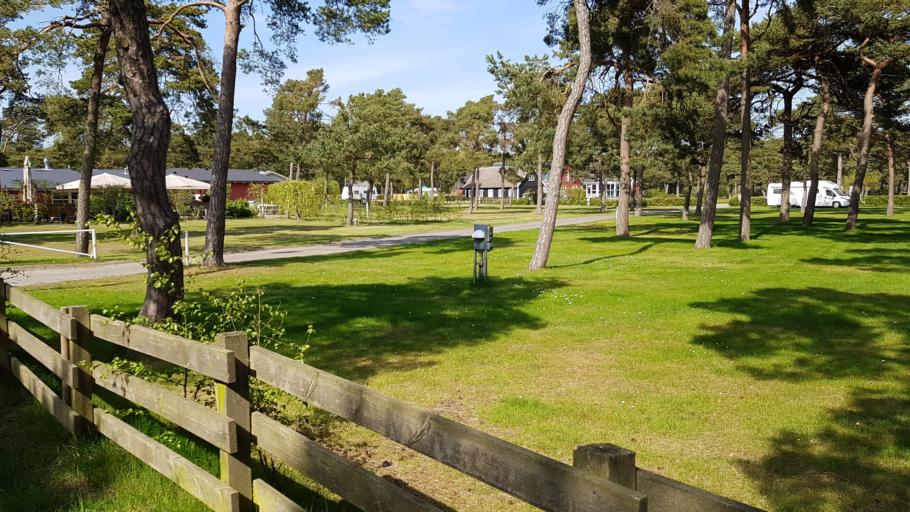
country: DK
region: Capital Region
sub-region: Bornholm Kommune
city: Nexo
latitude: 54.9960
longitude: 15.0866
